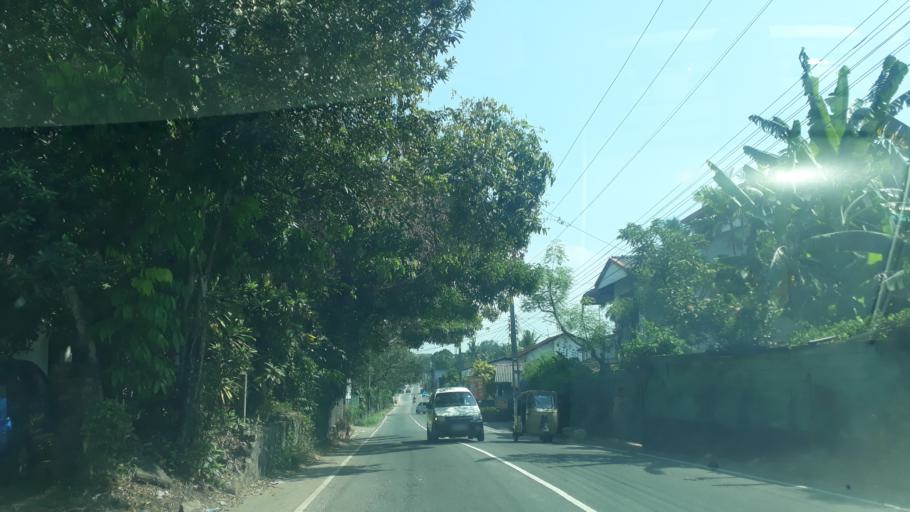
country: LK
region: Western
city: Gampaha
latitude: 7.0792
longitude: 80.0124
